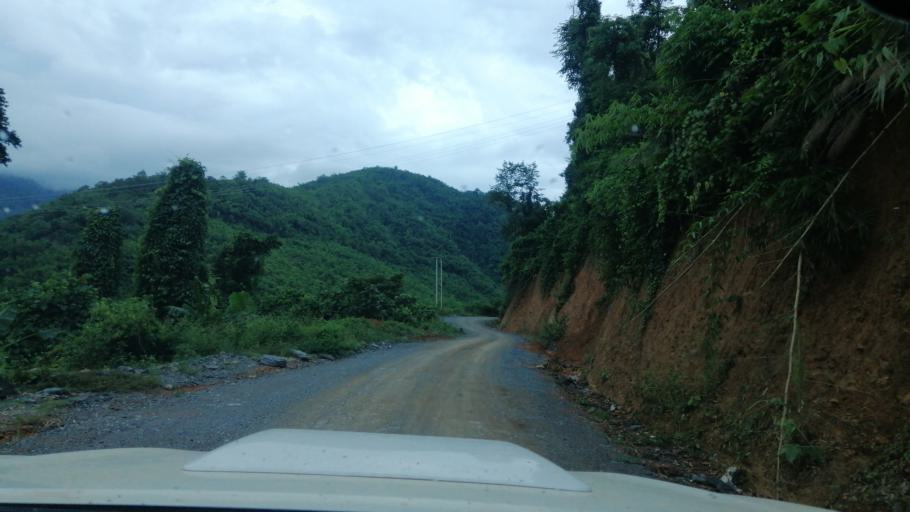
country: LA
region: Xiagnabouli
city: Sainyabuli
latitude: 19.1823
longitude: 101.7971
